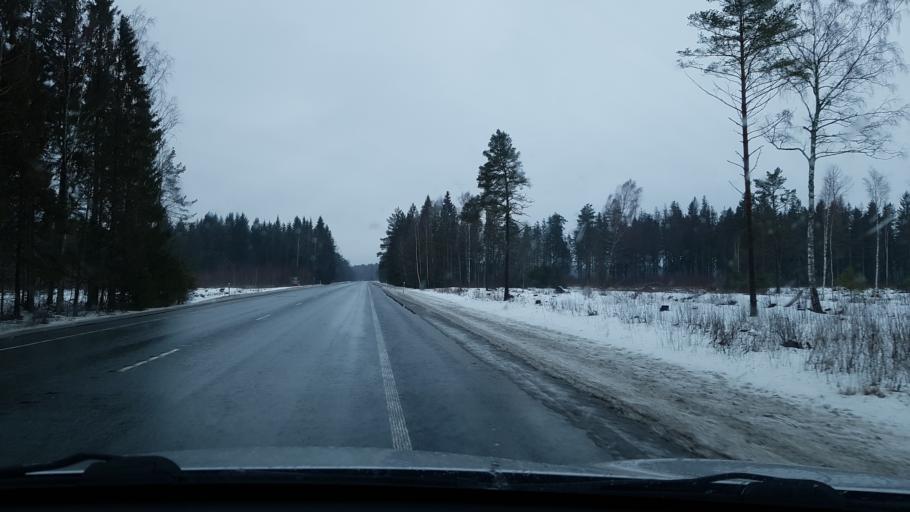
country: EE
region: Raplamaa
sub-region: Kohila vald
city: Kohila
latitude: 59.1547
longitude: 24.7784
